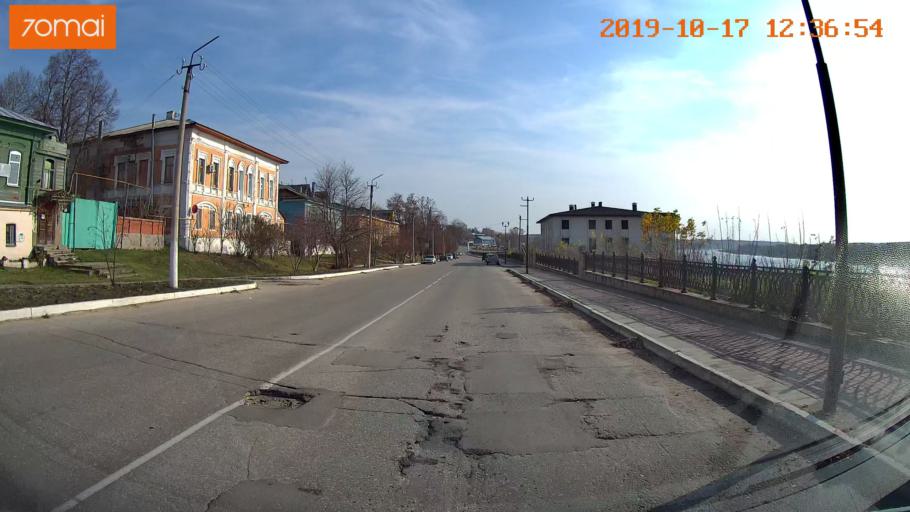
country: RU
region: Rjazan
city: Kasimov
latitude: 54.9384
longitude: 41.3809
